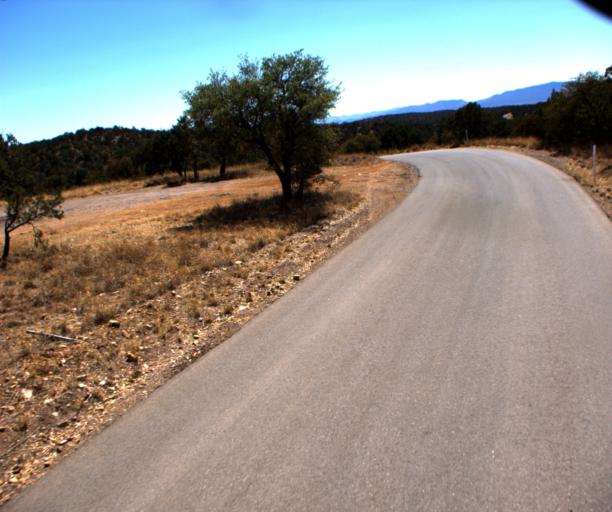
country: US
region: Arizona
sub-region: Cochise County
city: Sierra Vista
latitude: 31.4340
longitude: -110.4405
